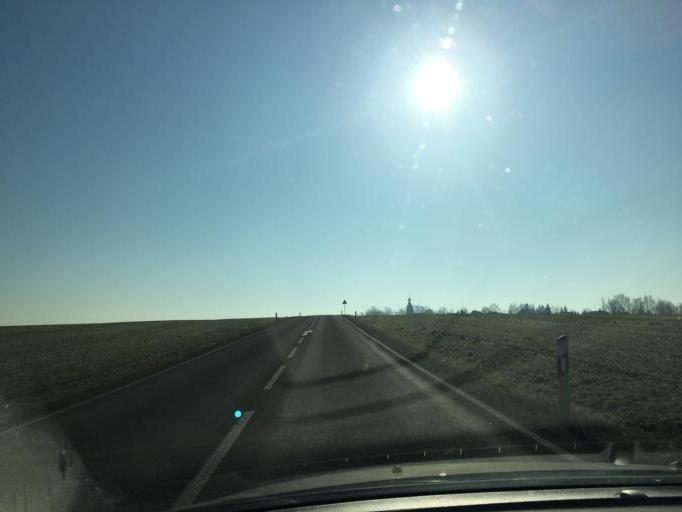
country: DE
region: Saxony
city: Otterwisch
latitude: 51.1797
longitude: 12.6181
